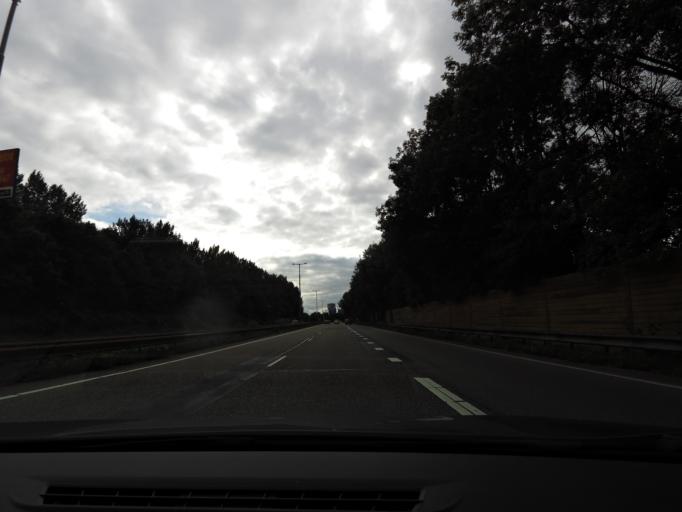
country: NL
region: Utrecht
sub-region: Gemeente Utrecht
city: Lunetten
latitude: 52.0615
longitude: 5.1245
